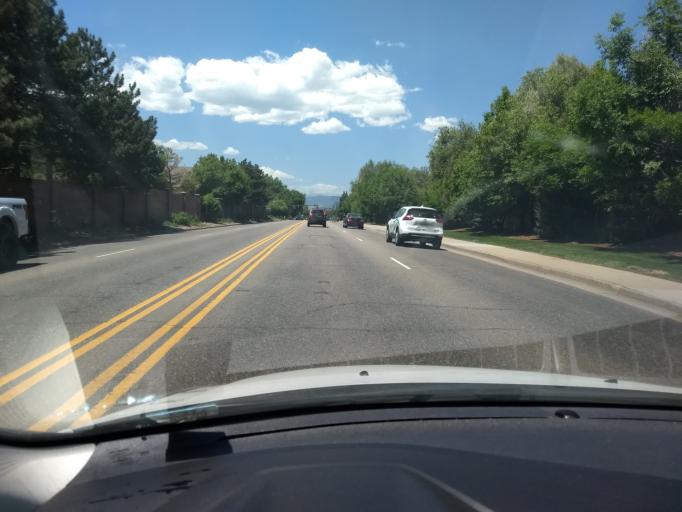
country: US
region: Colorado
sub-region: Arapahoe County
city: Cherry Hills Village
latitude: 39.6241
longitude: -104.9757
